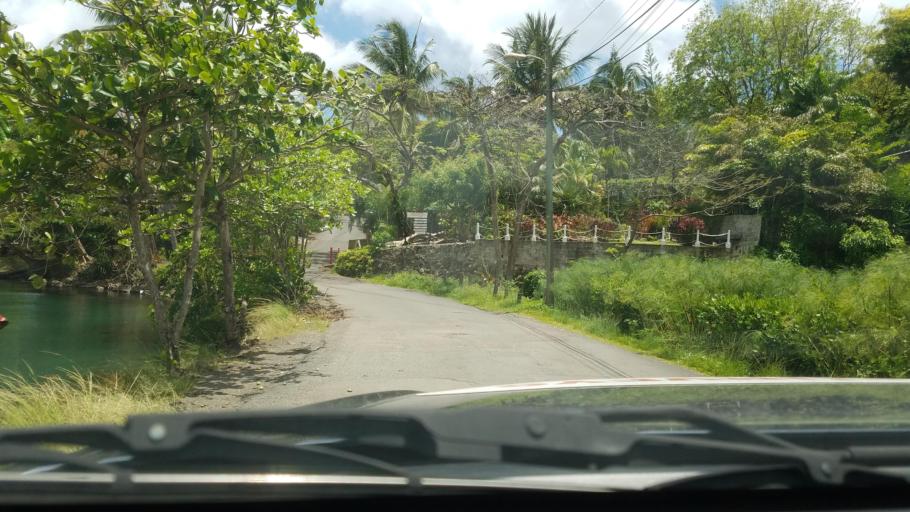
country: LC
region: Castries Quarter
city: Bisee
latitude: 14.0169
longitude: -60.9947
